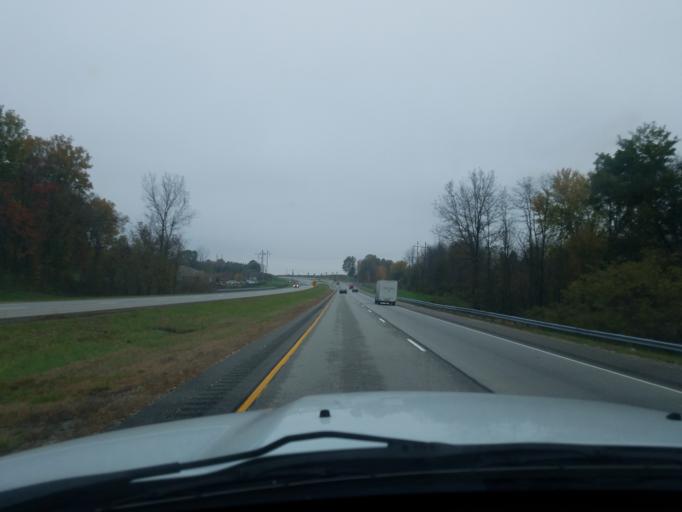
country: US
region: Kentucky
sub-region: Hardin County
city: Elizabethtown
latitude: 37.6625
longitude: -85.8381
